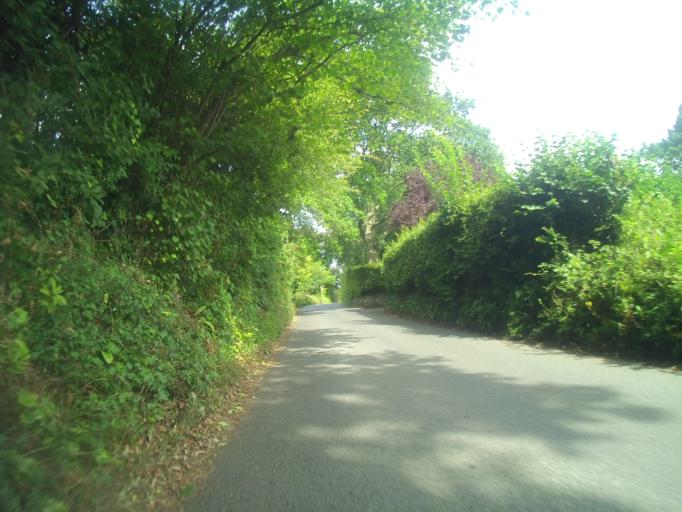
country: GB
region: England
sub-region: Devon
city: Totnes
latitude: 50.4398
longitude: -3.7053
